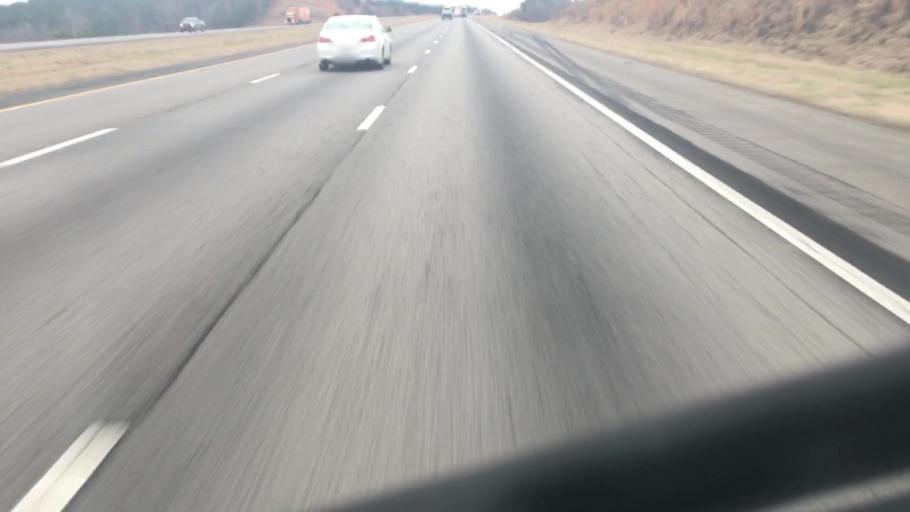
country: US
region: Alabama
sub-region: Walker County
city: Dora
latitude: 33.6870
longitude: -87.1074
